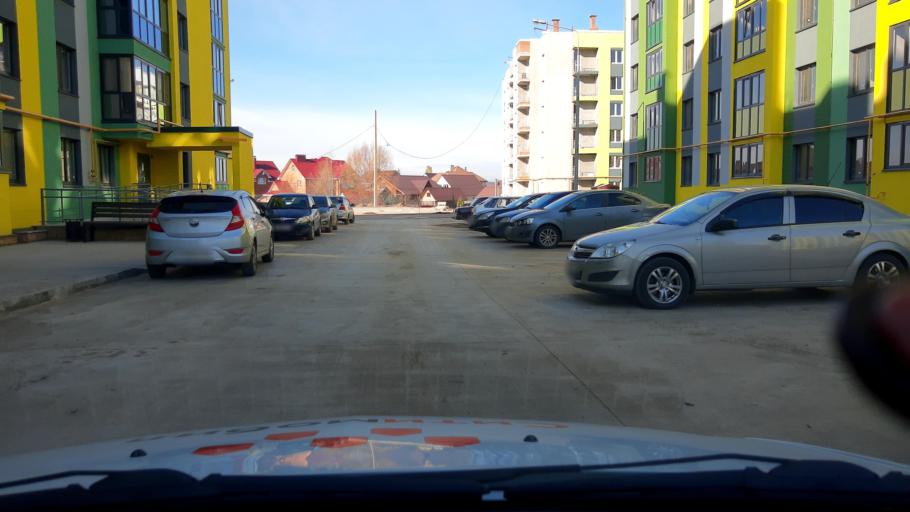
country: RU
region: Bashkortostan
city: Ufa
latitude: 54.7961
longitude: 55.9514
